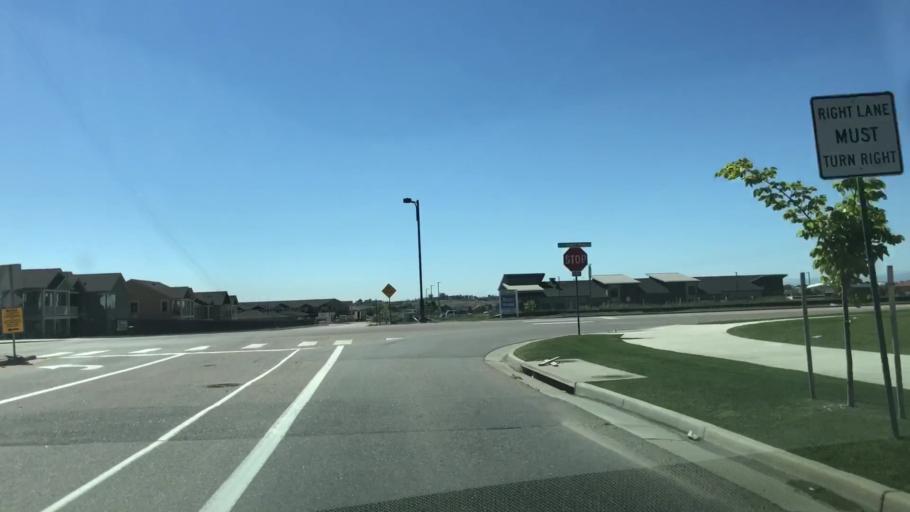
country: US
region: Colorado
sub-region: Weld County
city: Johnstown
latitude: 40.4039
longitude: -104.9740
